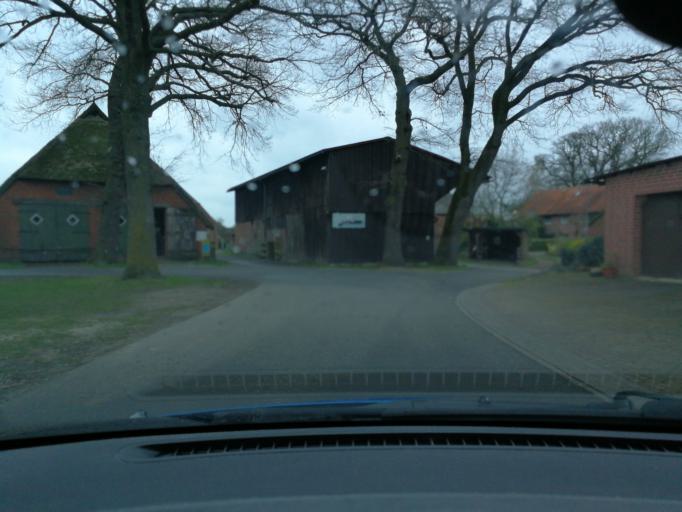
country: DE
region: Lower Saxony
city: Wittorf
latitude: 53.3321
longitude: 10.3802
